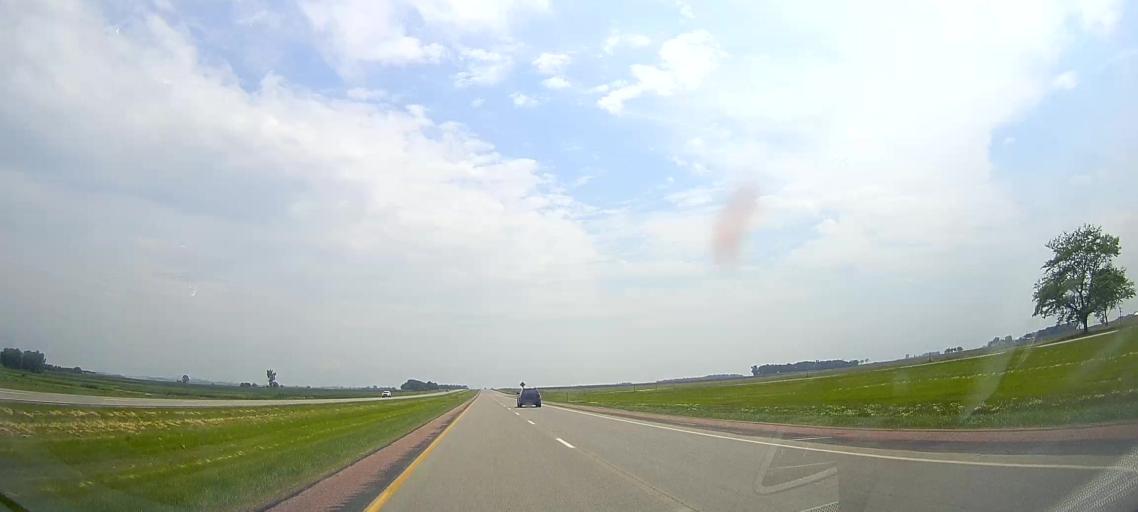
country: US
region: South Dakota
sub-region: Union County
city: Beresford
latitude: 42.9883
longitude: -96.7954
